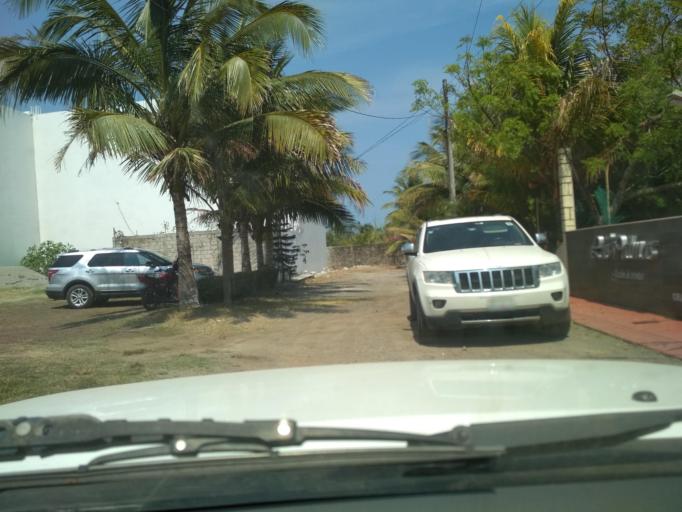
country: MX
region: Veracruz
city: Boca del Rio
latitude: 19.0985
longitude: -96.1141
